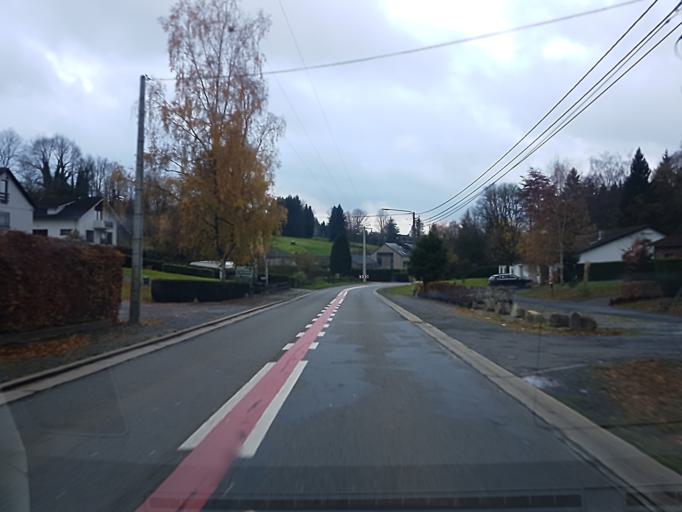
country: BE
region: Wallonia
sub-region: Province de Liege
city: Theux
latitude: 50.5396
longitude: 5.8252
